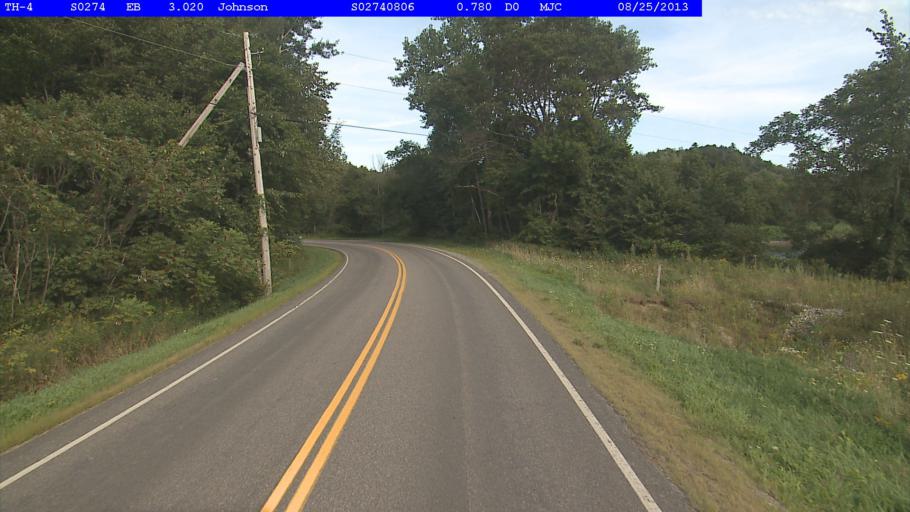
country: US
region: Vermont
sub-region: Lamoille County
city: Johnson
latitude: 44.6525
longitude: -72.7365
